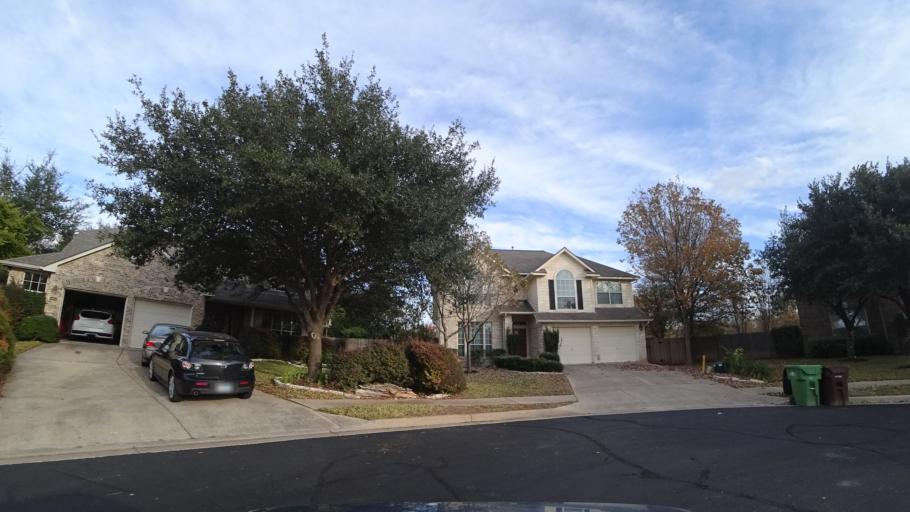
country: US
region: Texas
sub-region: Williamson County
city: Brushy Creek
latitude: 30.5177
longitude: -97.7327
